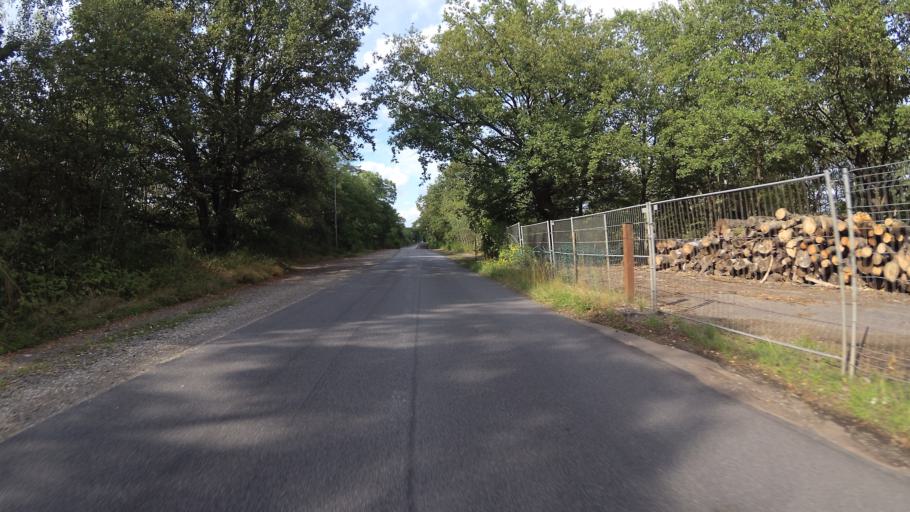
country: DE
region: Saarland
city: Homburg
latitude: 49.3075
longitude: 7.3181
